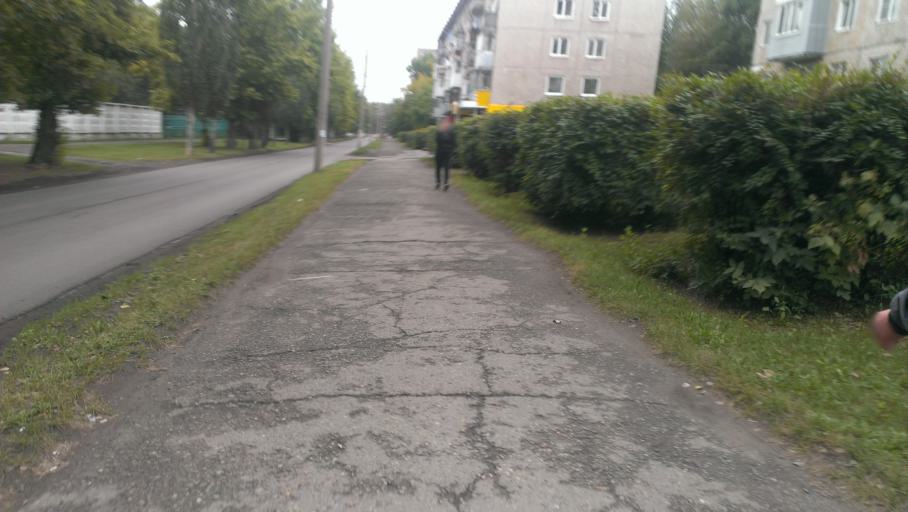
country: RU
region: Altai Krai
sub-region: Gorod Barnaulskiy
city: Barnaul
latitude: 53.3689
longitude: 83.6897
